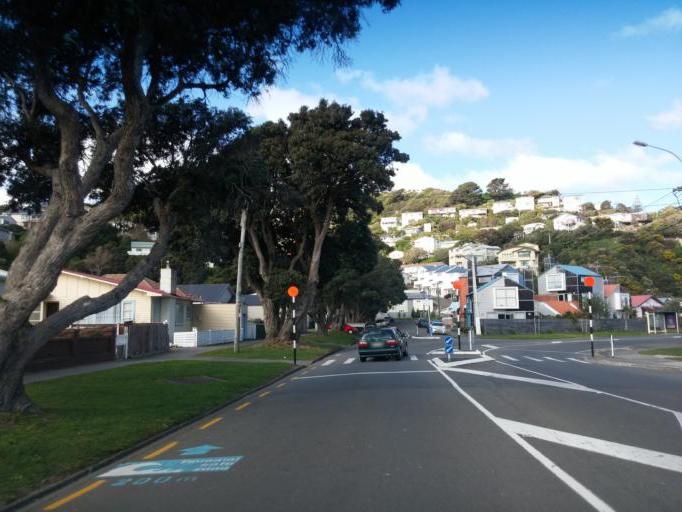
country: NZ
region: Wellington
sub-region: Wellington City
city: Wellington
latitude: -41.3176
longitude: 174.8193
